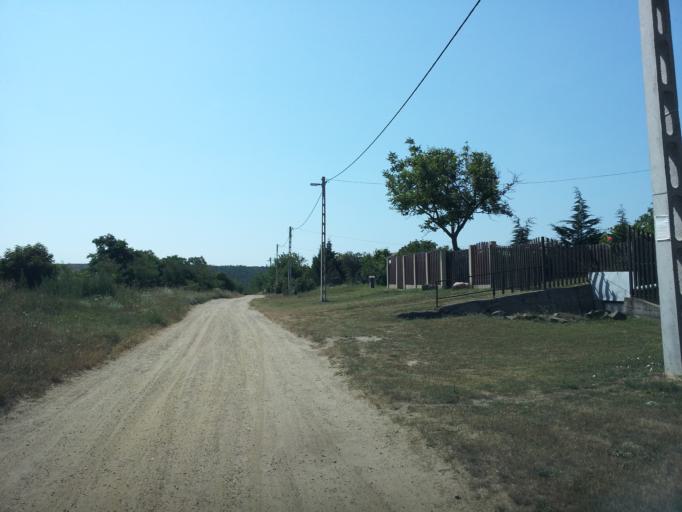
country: HU
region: Fejer
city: Pakozd
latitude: 47.2602
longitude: 18.5093
